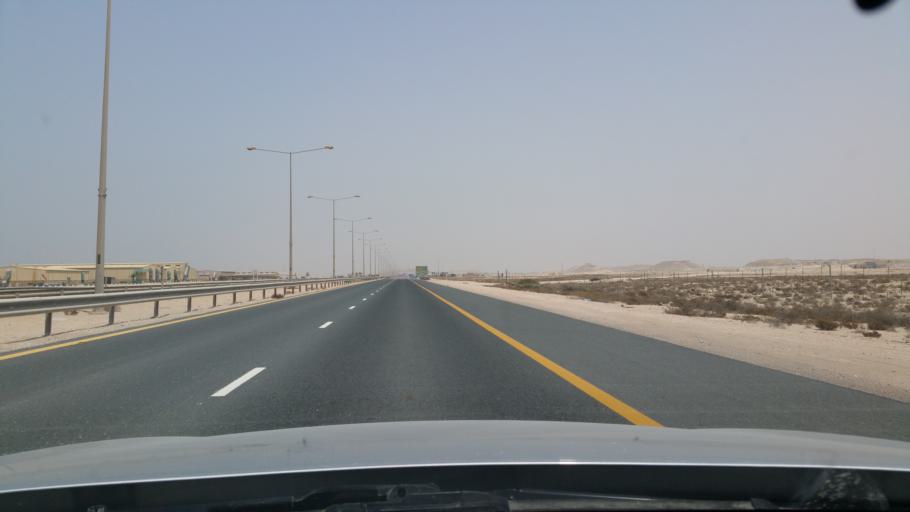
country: QA
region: Baladiyat ar Rayyan
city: Dukhan
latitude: 25.3750
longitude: 50.7811
